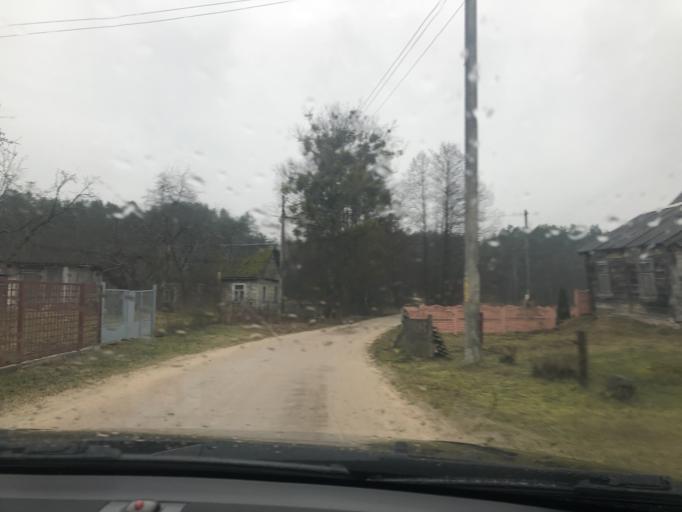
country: BY
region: Grodnenskaya
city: Skidal'
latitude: 53.8588
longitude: 24.2415
